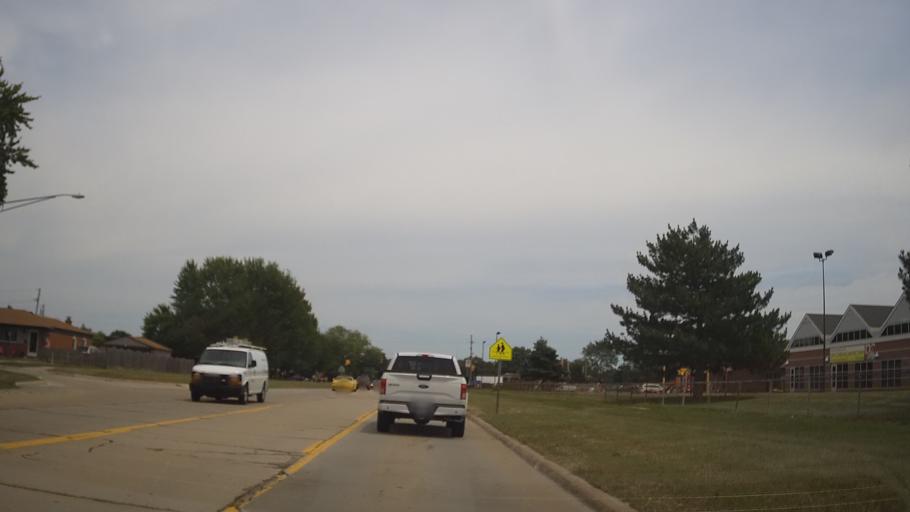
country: US
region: Michigan
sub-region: Macomb County
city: Sterling Heights
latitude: 42.5808
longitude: -83.0136
